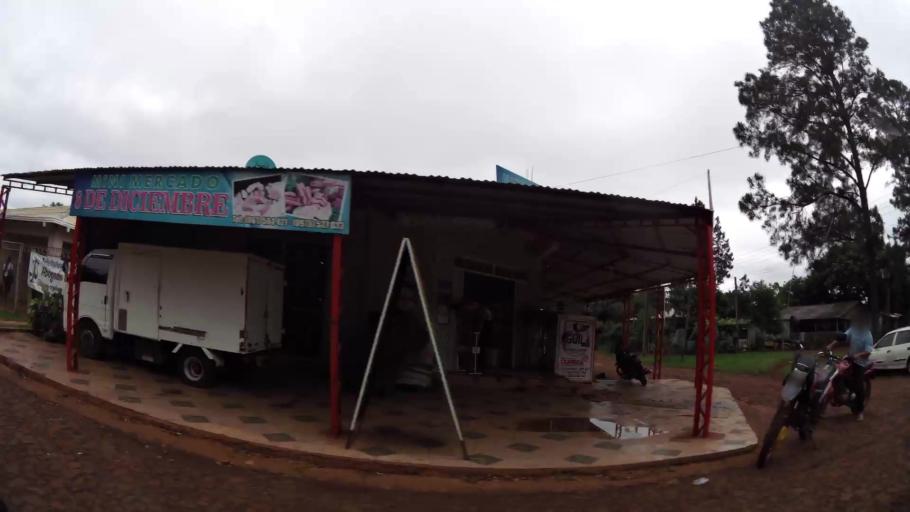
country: PY
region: Alto Parana
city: Presidente Franco
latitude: -25.4869
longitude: -54.7968
